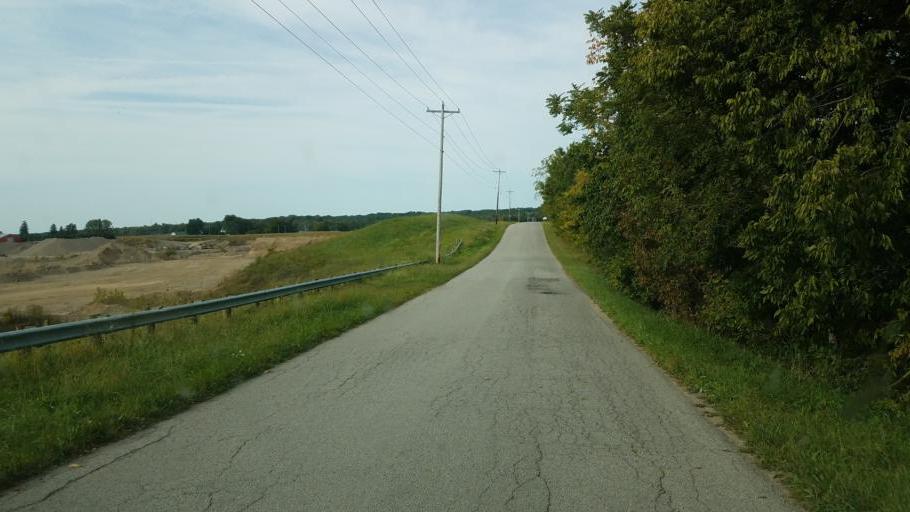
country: US
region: Ohio
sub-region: Knox County
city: Fredericktown
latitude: 40.4655
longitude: -82.6559
